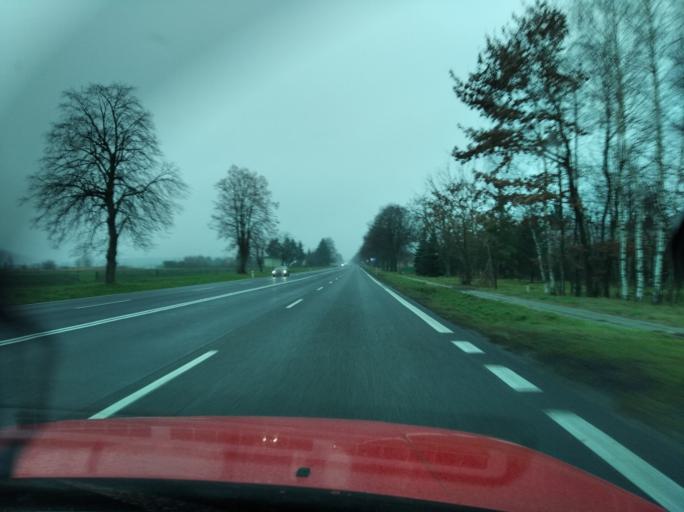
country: PL
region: Subcarpathian Voivodeship
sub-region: Powiat przeworski
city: Grzeska
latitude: 50.0626
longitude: 22.4548
